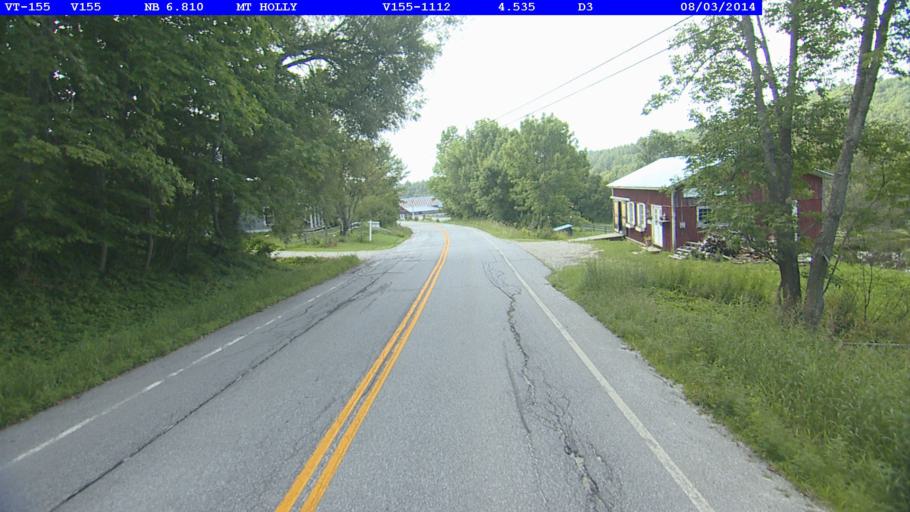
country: US
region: Vermont
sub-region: Rutland County
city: Rutland
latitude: 43.4112
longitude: -72.8443
